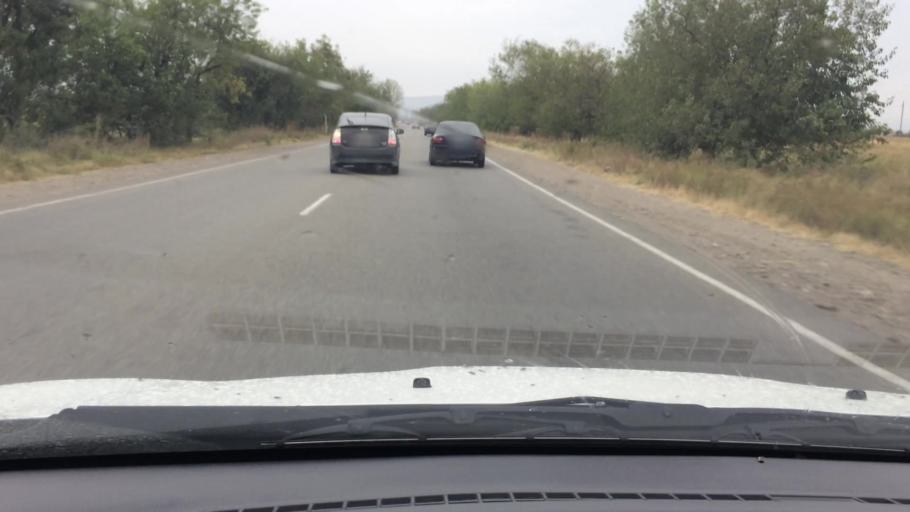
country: GE
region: Kvemo Kartli
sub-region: Marneuli
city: Marneuli
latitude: 41.5640
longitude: 44.7756
